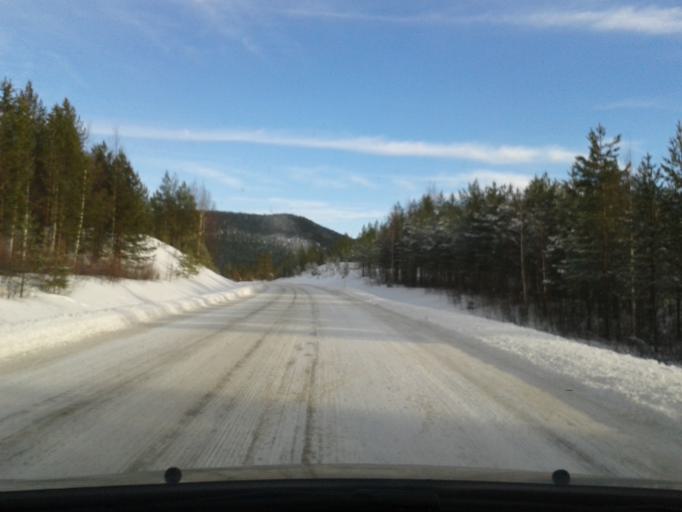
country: SE
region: Vaesterbotten
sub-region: Asele Kommun
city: Asele
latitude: 64.3154
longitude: 17.1813
